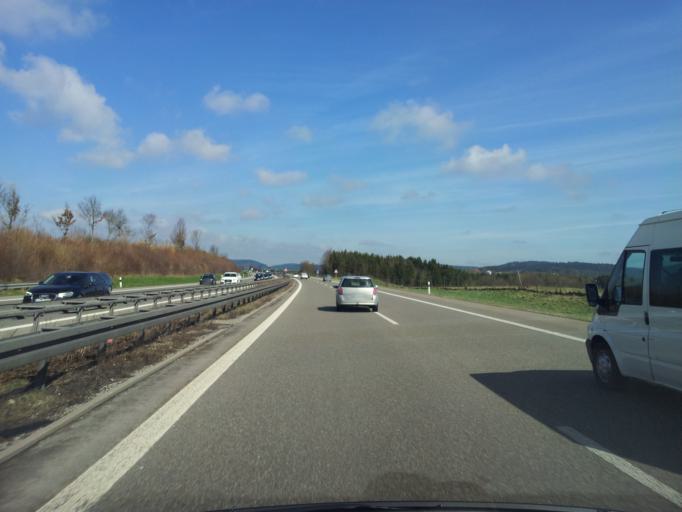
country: DE
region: Baden-Wuerttemberg
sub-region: Freiburg Region
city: Dietingen
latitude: 48.2339
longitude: 8.6505
